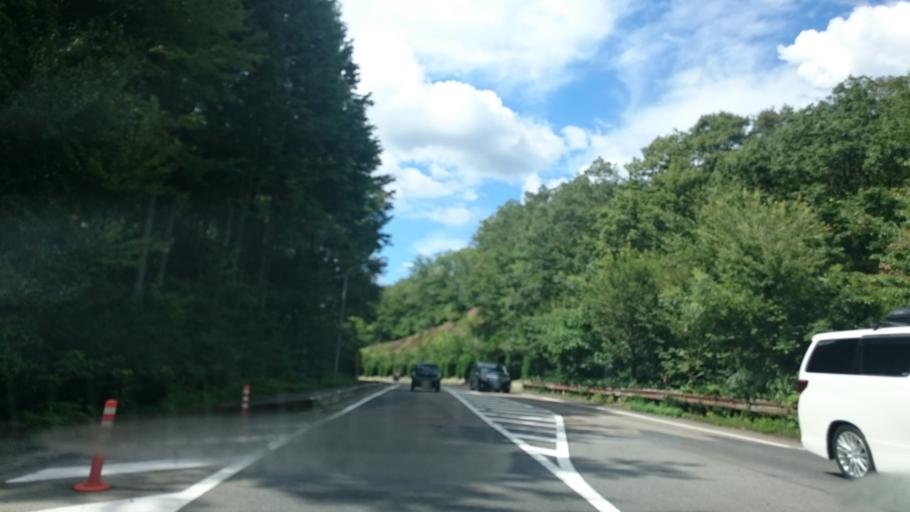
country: JP
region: Gifu
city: Nakatsugawa
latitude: 35.5048
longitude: 137.4778
